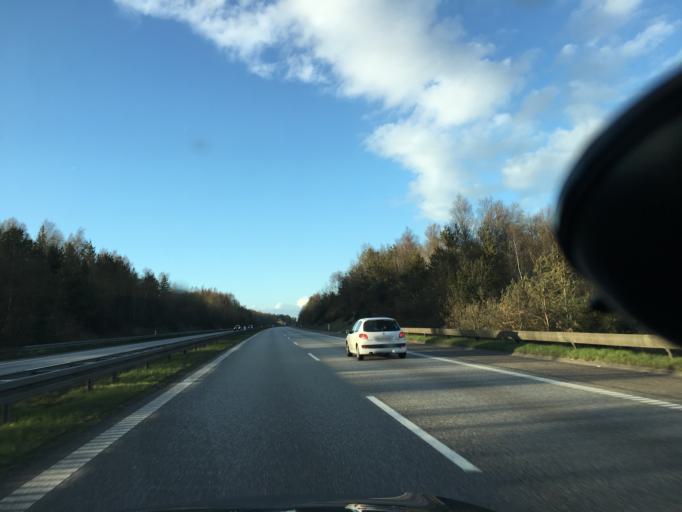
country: DK
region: North Denmark
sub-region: Rebild Kommune
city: Stovring
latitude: 56.9177
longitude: 9.8424
